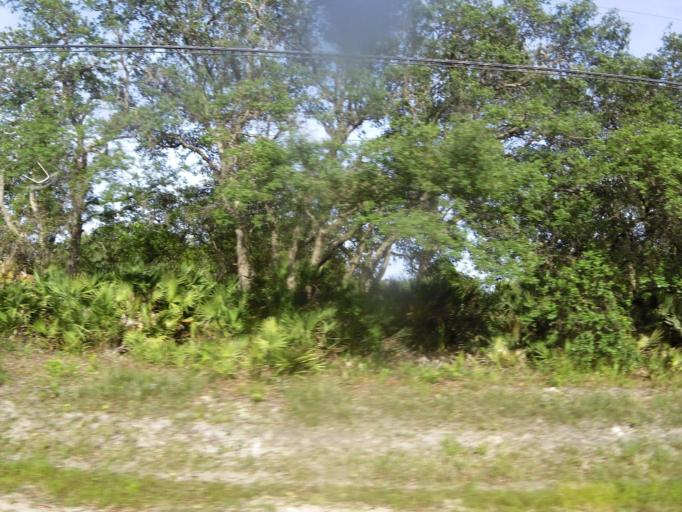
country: US
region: Florida
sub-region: Duval County
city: Atlantic Beach
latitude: 30.4699
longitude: -81.4696
